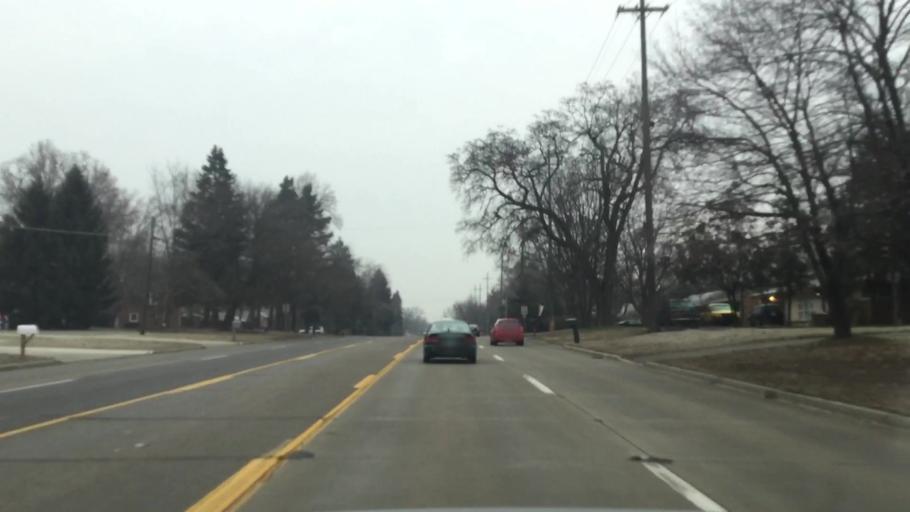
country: US
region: Michigan
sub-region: Oakland County
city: Farmington
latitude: 42.4211
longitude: -83.3551
